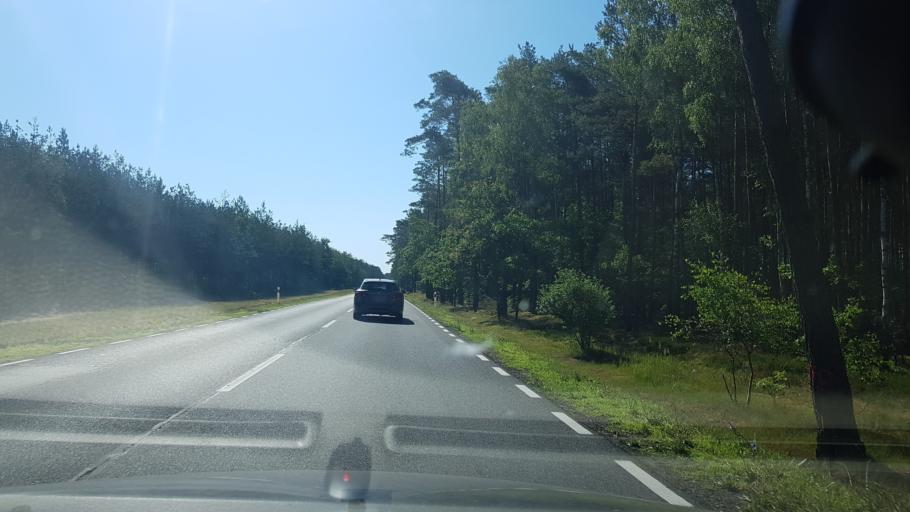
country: PL
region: Masovian Voivodeship
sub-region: Powiat wyszkowski
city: Branszczyk
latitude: 52.5619
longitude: 21.5696
